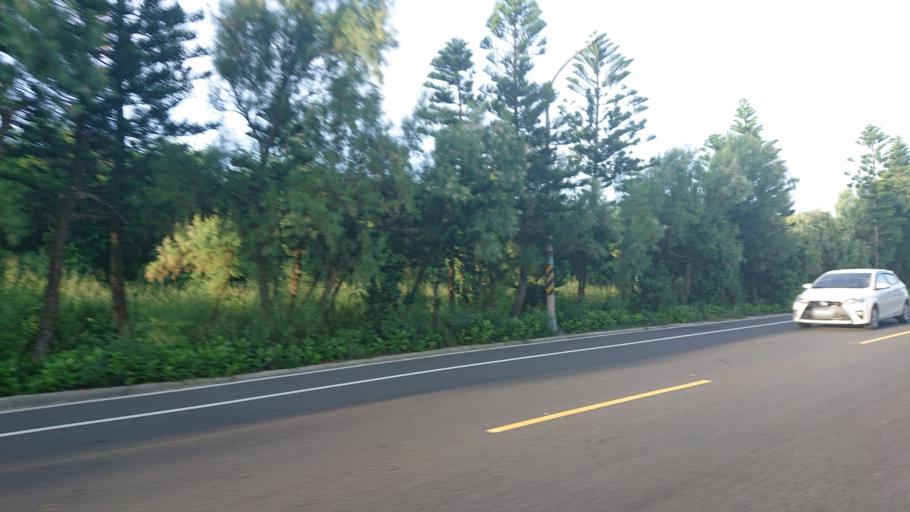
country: TW
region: Taiwan
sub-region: Penghu
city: Ma-kung
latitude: 23.6625
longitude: 119.5787
